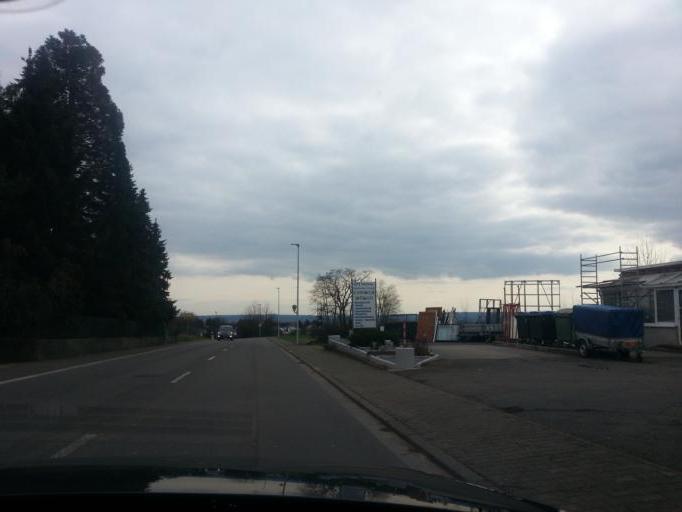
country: DE
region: Saarland
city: Bexbach
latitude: 49.3738
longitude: 7.2654
